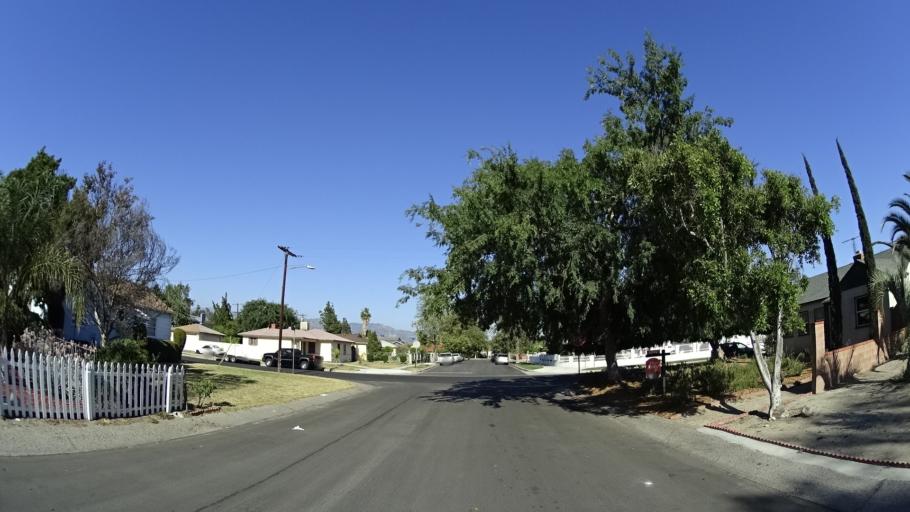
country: US
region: California
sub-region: Los Angeles County
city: North Hollywood
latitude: 34.1821
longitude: -118.3773
